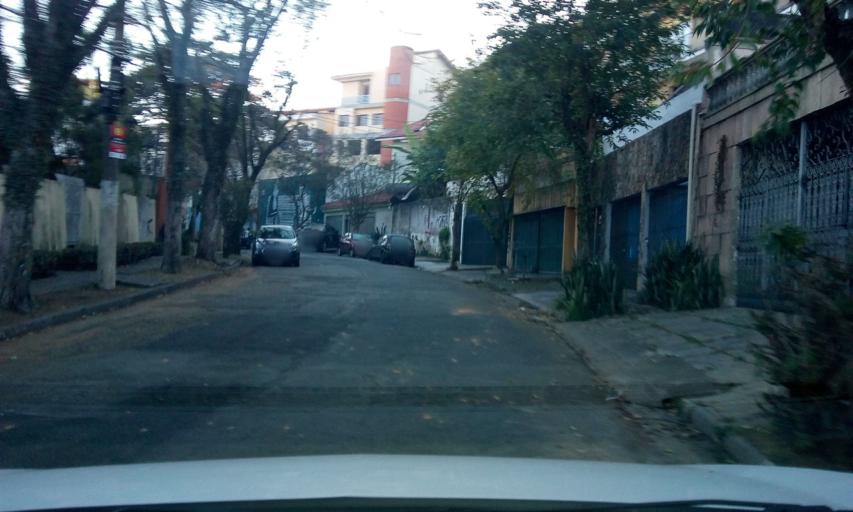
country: BR
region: Sao Paulo
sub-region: Sao Paulo
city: Sao Paulo
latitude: -23.5390
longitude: -46.7001
